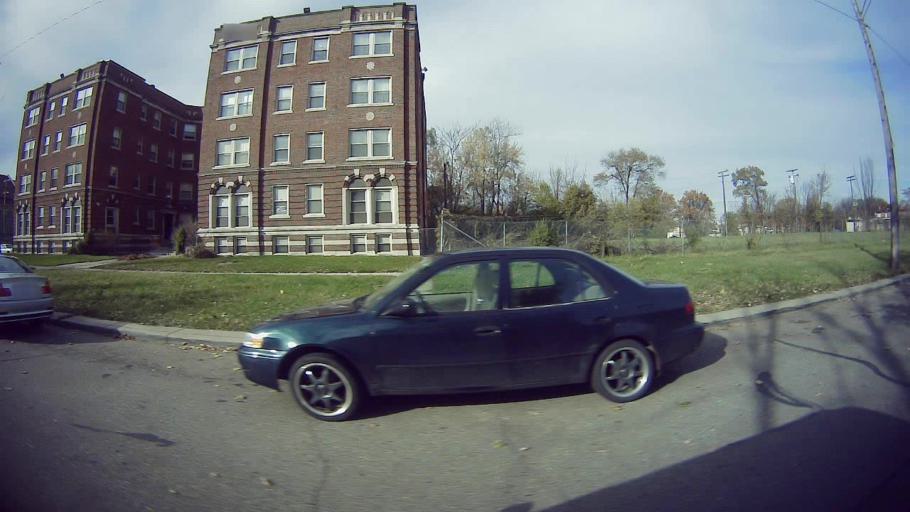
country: US
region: Michigan
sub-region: Wayne County
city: Highland Park
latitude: 42.3760
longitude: -83.1127
